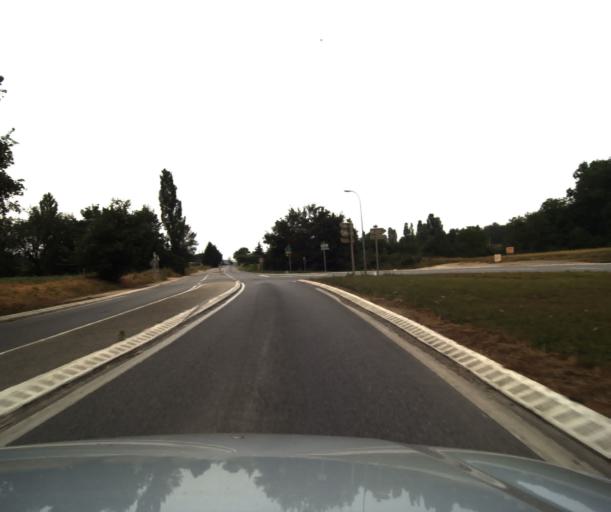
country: FR
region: Midi-Pyrenees
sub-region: Departement du Gers
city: Gimont
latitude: 43.7247
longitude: 0.8739
